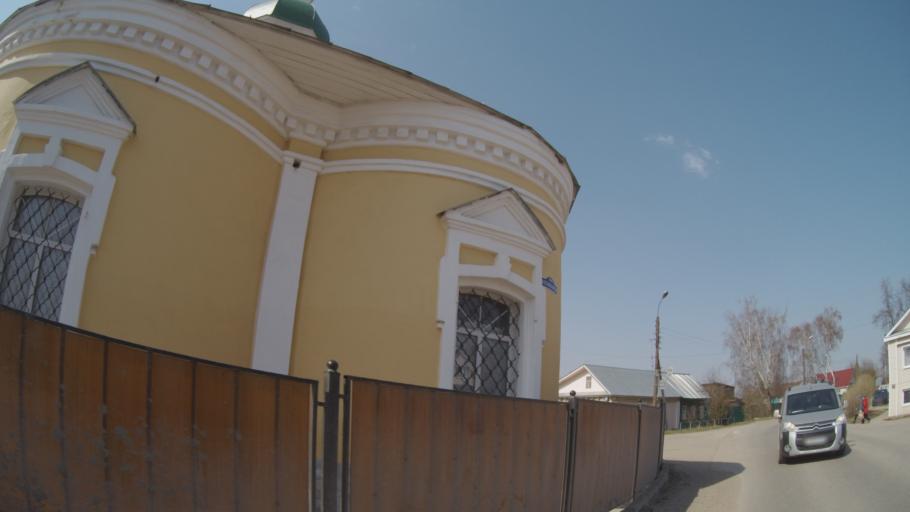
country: RU
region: Nizjnij Novgorod
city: Arzamas
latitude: 55.3867
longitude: 43.8238
